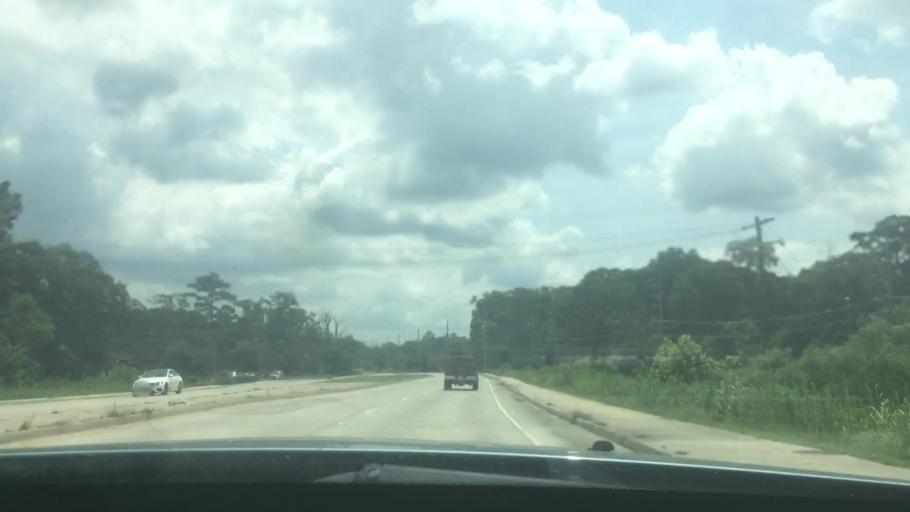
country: US
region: Louisiana
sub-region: East Baton Rouge Parish
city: Shenandoah
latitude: 30.4237
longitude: -91.0137
